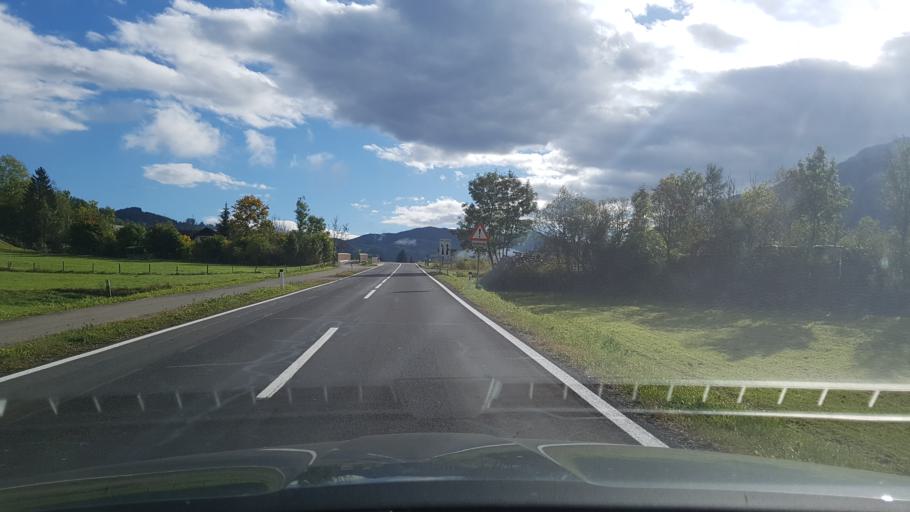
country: AT
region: Styria
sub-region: Politischer Bezirk Murau
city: Sankt Peter am Kammersberg
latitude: 47.1883
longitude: 14.1556
